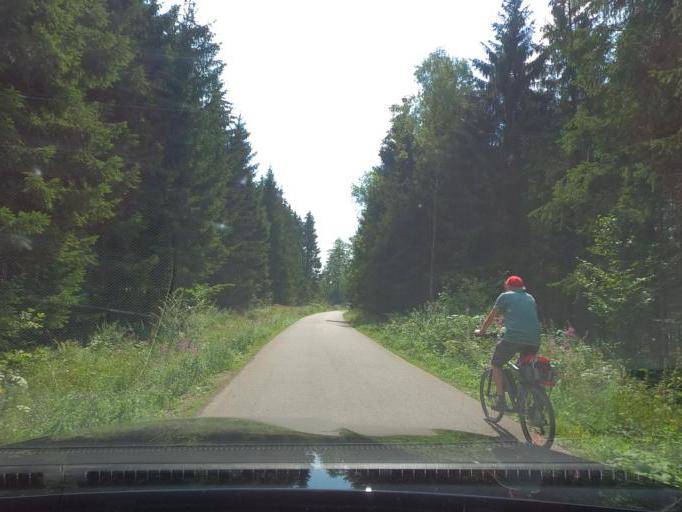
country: DE
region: Lower Saxony
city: Clausthal-Zellerfeld
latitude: 51.7698
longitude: 10.3066
